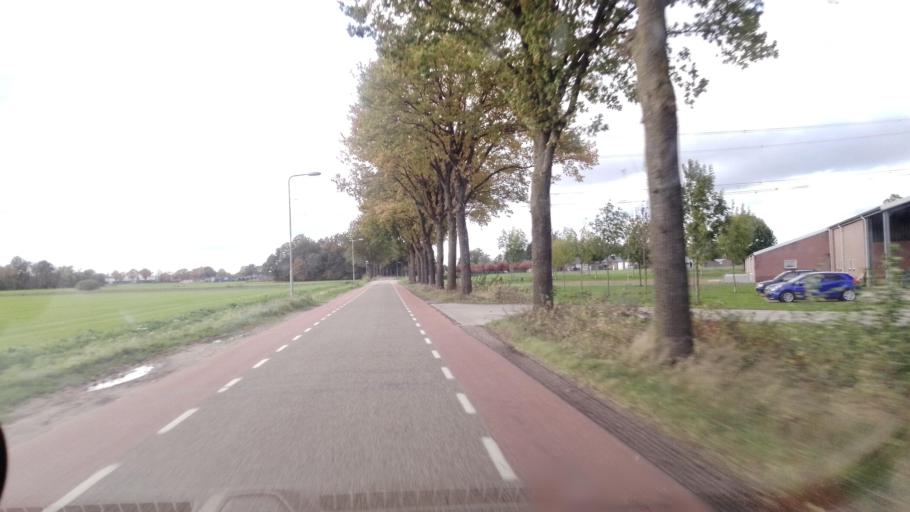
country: NL
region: Limburg
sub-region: Gemeente Venray
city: Venray
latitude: 51.4957
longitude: 5.9266
